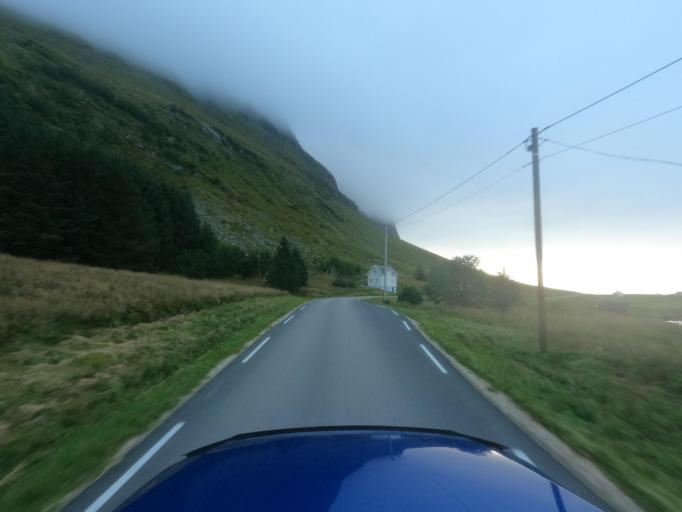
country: NO
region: Nordland
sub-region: Vestvagoy
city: Evjen
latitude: 68.2829
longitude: 13.7185
